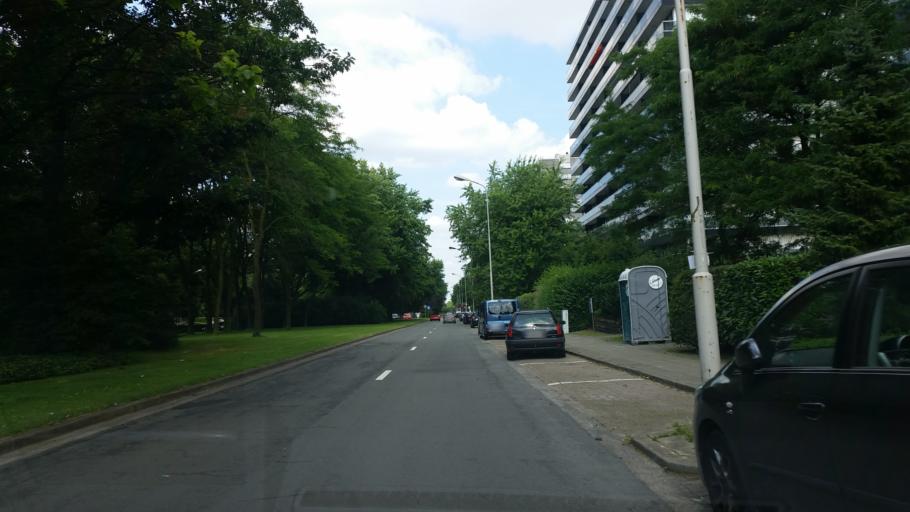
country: BE
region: Flanders
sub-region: Provincie Antwerpen
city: Mortsel
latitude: 51.1833
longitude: 4.4394
